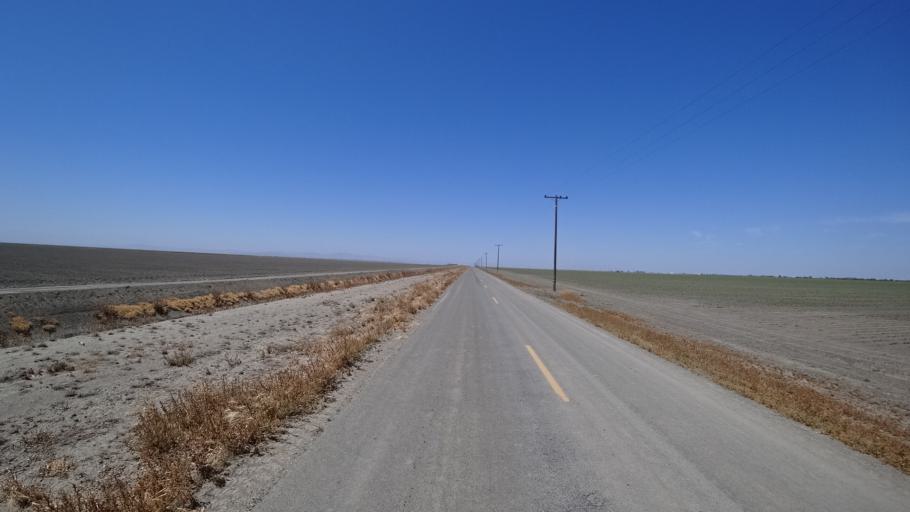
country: US
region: California
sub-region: Kings County
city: Stratford
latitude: 36.1234
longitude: -119.7186
